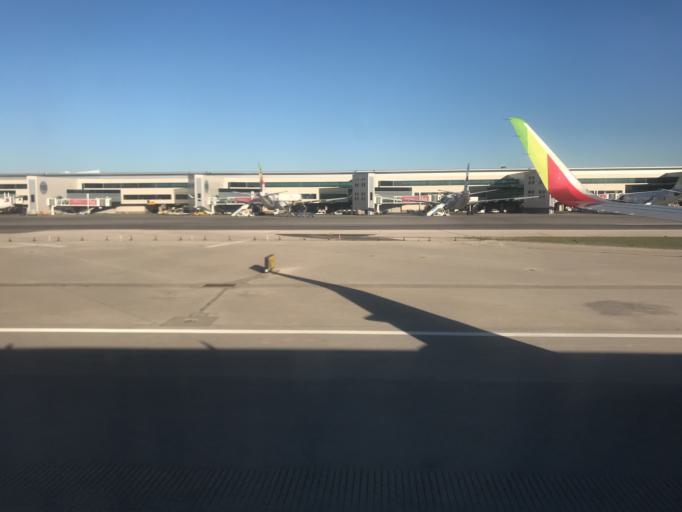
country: PT
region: Lisbon
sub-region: Loures
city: Camarate
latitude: 38.7747
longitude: -9.1340
